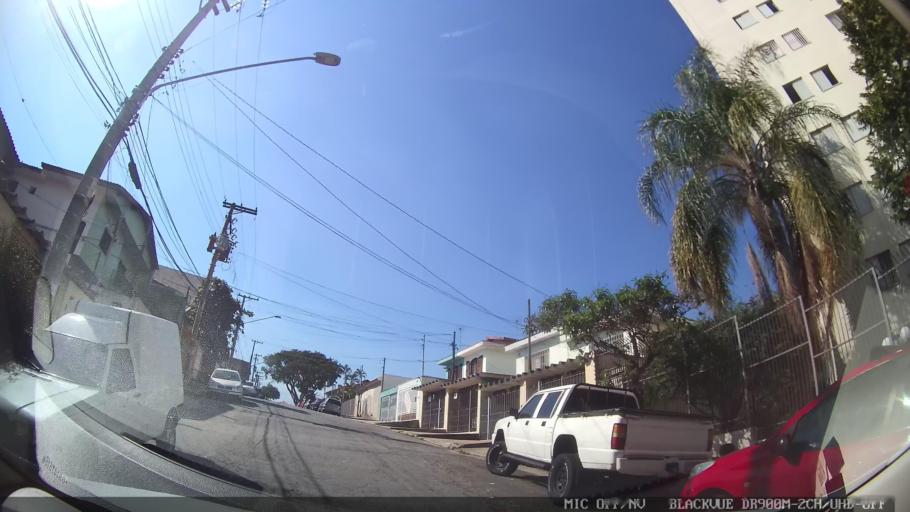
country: BR
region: Sao Paulo
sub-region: Sao Paulo
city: Sao Paulo
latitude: -23.5072
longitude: -46.6631
